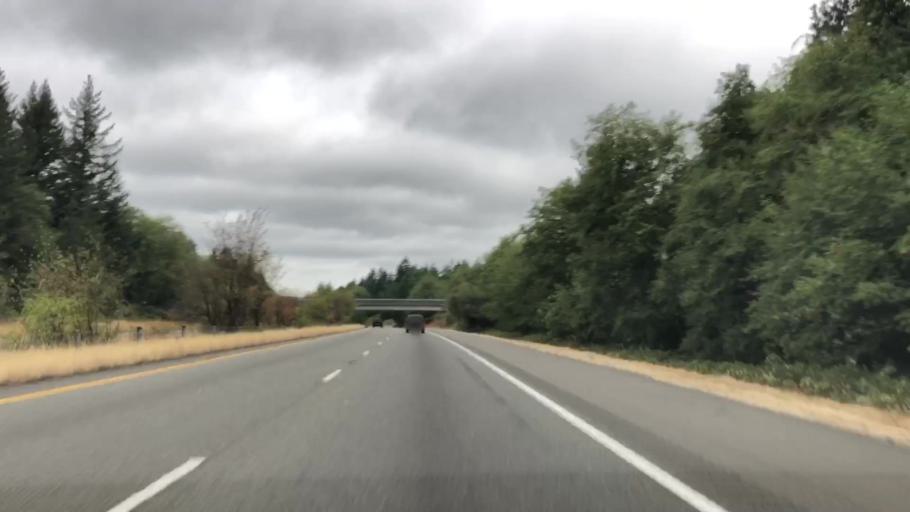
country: US
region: Washington
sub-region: Pierce County
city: Purdy
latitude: 47.3868
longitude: -122.6156
